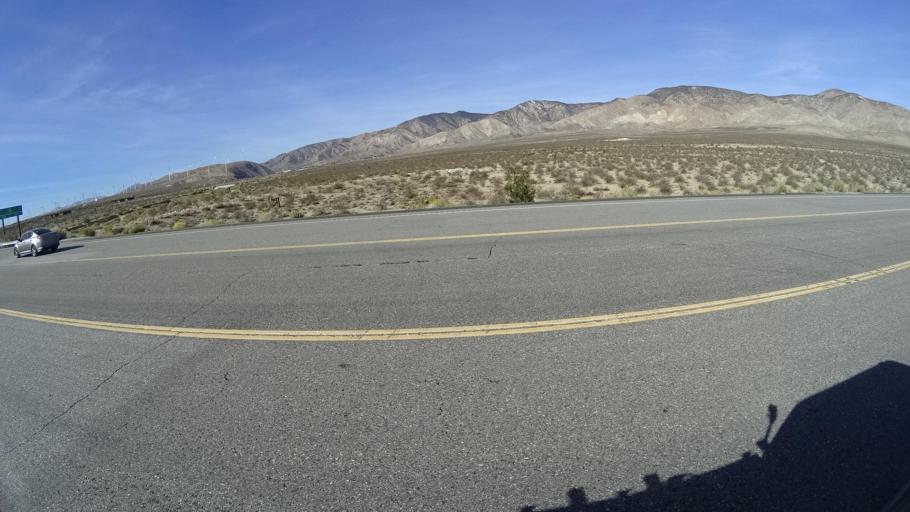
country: US
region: California
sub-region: Kern County
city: Mojave
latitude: 35.1190
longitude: -118.1762
